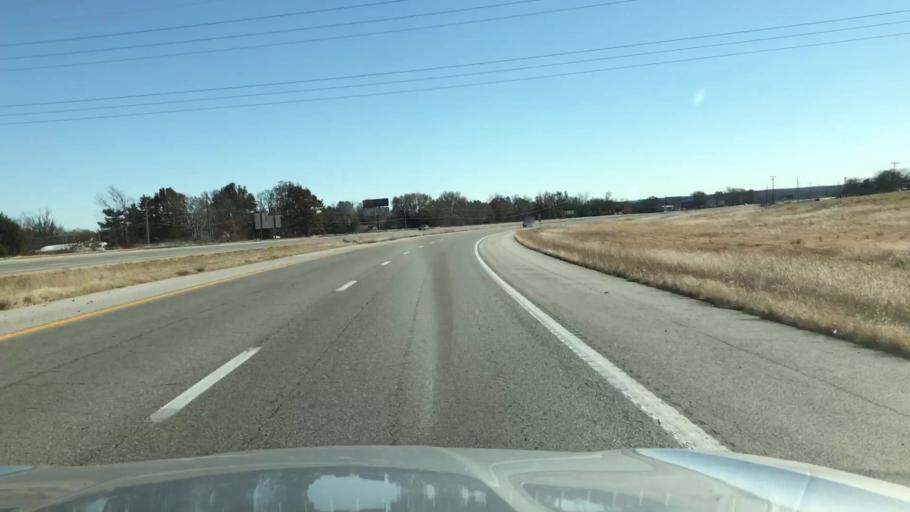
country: US
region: Missouri
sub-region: Jasper County
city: Carthage
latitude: 37.1315
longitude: -94.3124
